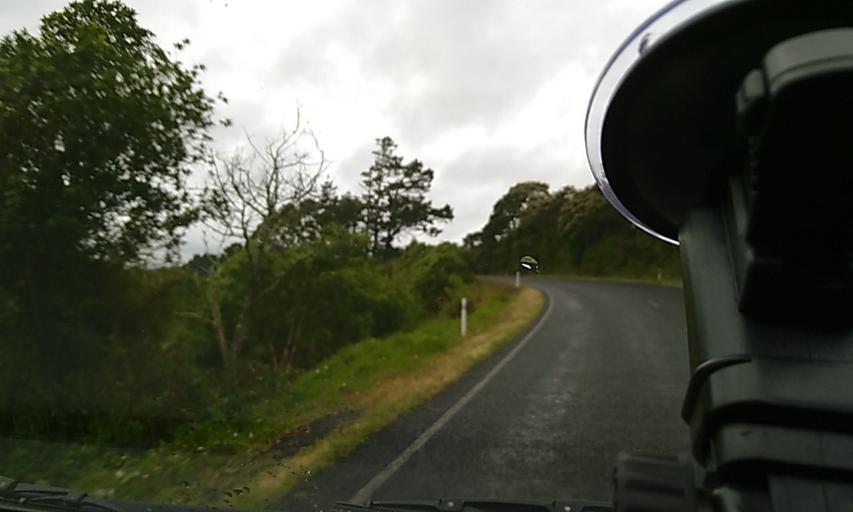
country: NZ
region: Auckland
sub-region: Auckland
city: Pukekohe East
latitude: -37.3209
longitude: 174.9290
